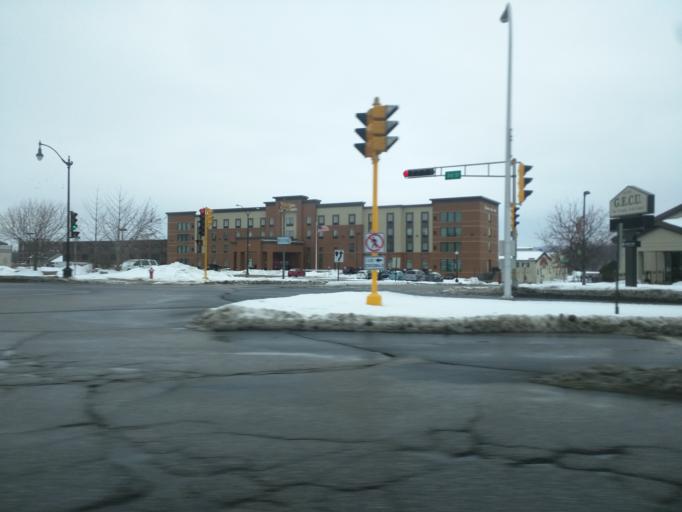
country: US
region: Wisconsin
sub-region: La Crosse County
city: La Crosse
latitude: 43.8174
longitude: -91.2490
